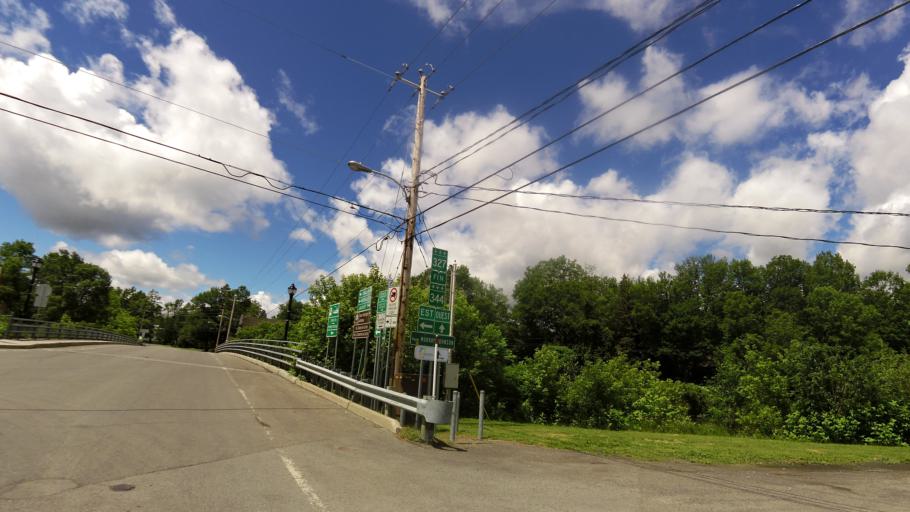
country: CA
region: Quebec
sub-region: Laurentides
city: Lachute
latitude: 45.5628
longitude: -74.3361
